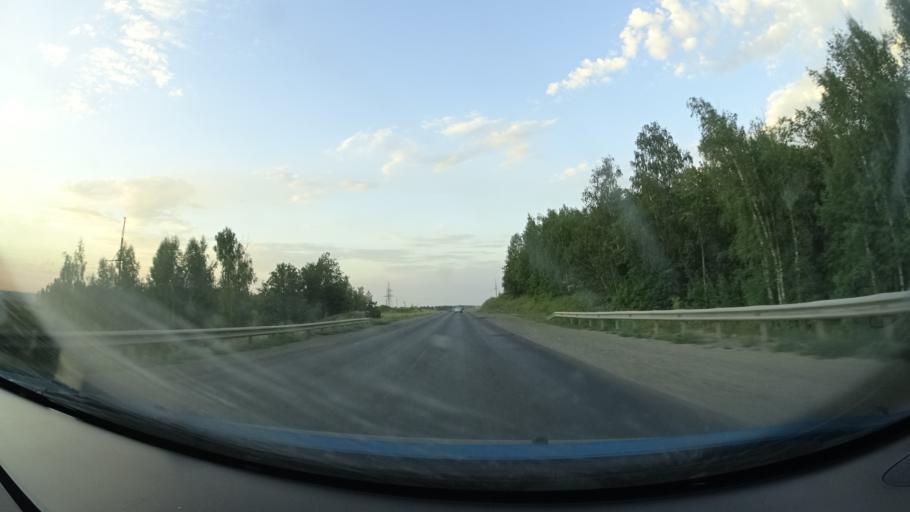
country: RU
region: Orenburg
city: Severnoye
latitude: 54.1785
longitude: 52.6557
